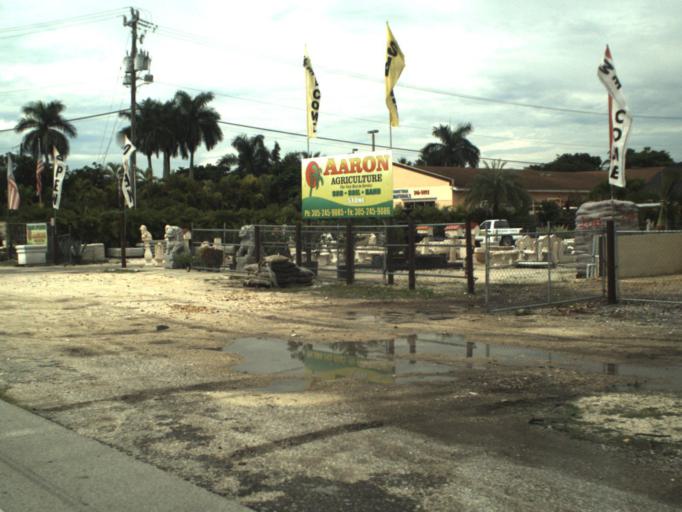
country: US
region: Florida
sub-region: Miami-Dade County
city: Naranja
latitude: 25.5573
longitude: -80.4782
